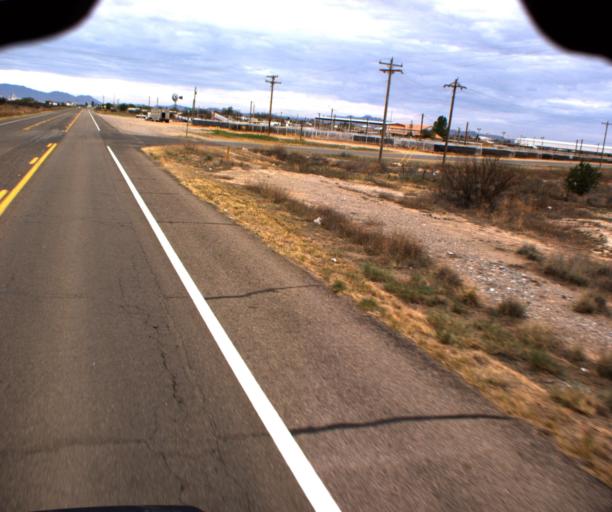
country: US
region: Arizona
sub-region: Cochise County
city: Willcox
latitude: 32.2683
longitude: -109.8217
